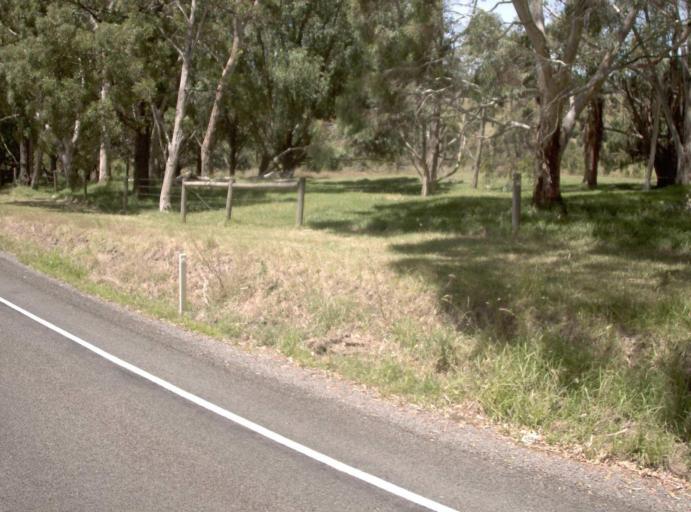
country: AU
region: Victoria
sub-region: Baw Baw
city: Warragul
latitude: -38.0729
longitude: 145.9028
